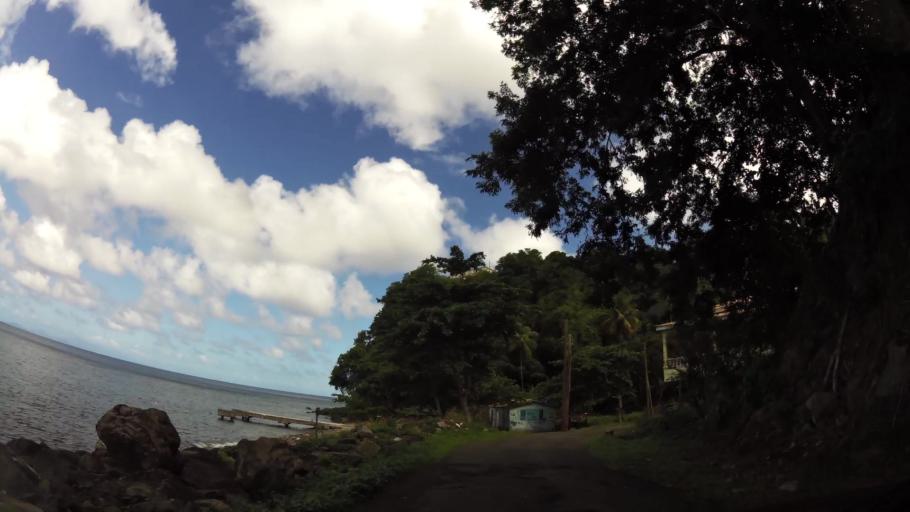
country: DM
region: Saint John
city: Portsmouth
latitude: 15.6288
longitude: -61.4636
